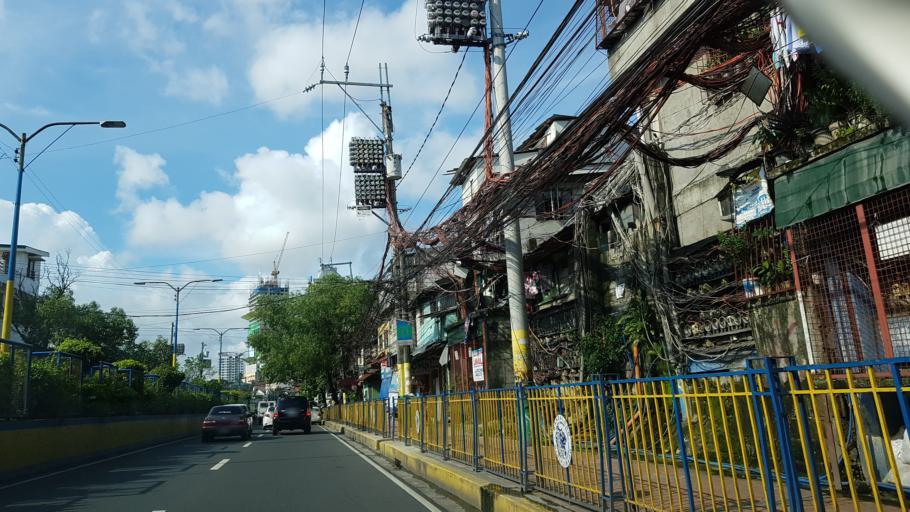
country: PH
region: Metro Manila
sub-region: Mandaluyong
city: Mandaluyong City
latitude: 14.5847
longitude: 121.0376
